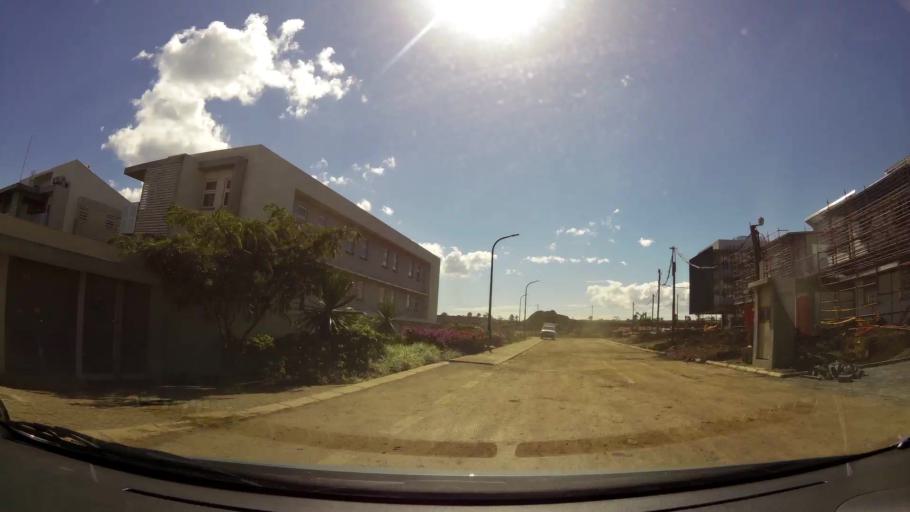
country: MU
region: Black River
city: Cascavelle
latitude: -20.2810
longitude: 57.3943
